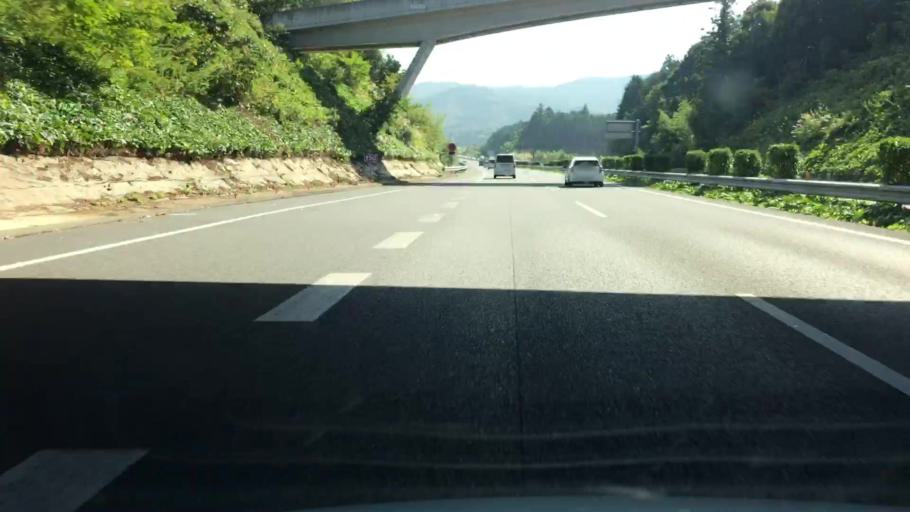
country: JP
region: Ibaraki
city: Iwase
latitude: 36.3448
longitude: 140.1774
